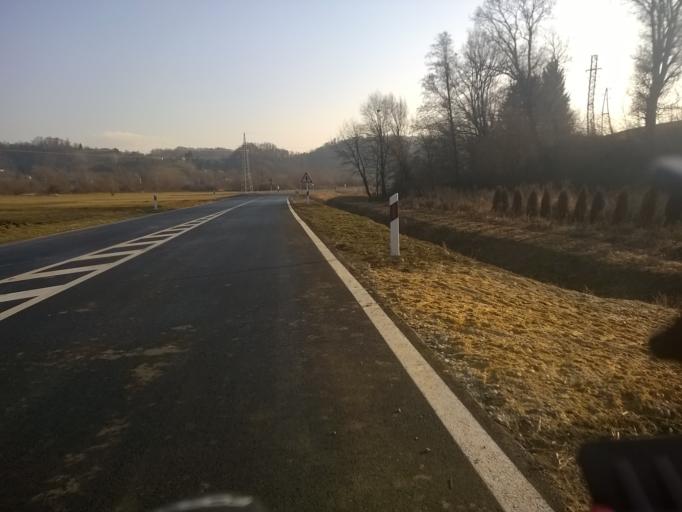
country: HR
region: Krapinsko-Zagorska
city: Zabok
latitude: 46.0367
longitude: 15.9199
